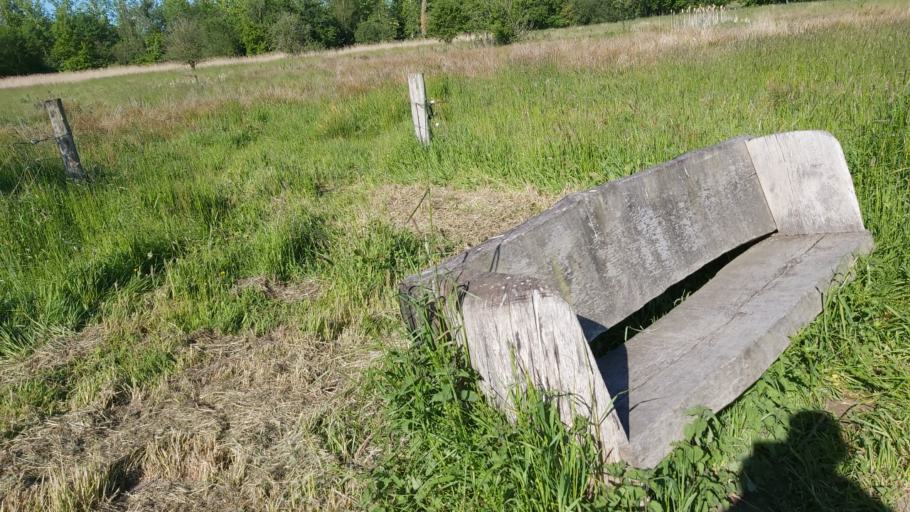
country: BE
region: Flanders
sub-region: Provincie Vlaams-Brabant
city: Boutersem
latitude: 50.8423
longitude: 4.8779
